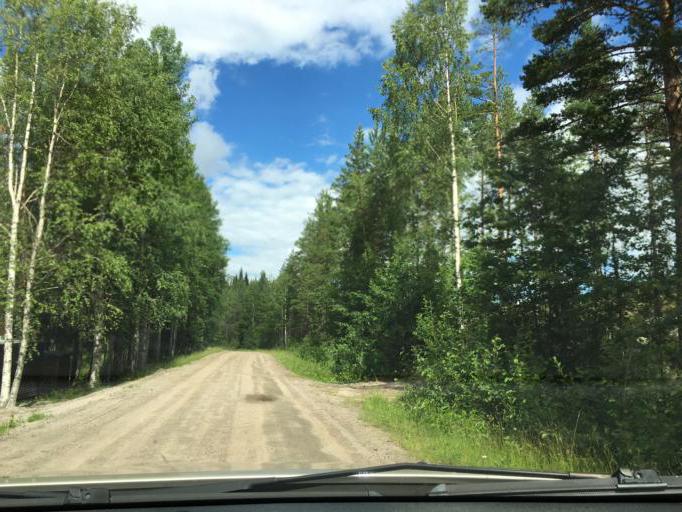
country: SE
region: Norrbotten
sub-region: Overkalix Kommun
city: OEverkalix
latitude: 66.1306
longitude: 22.7847
